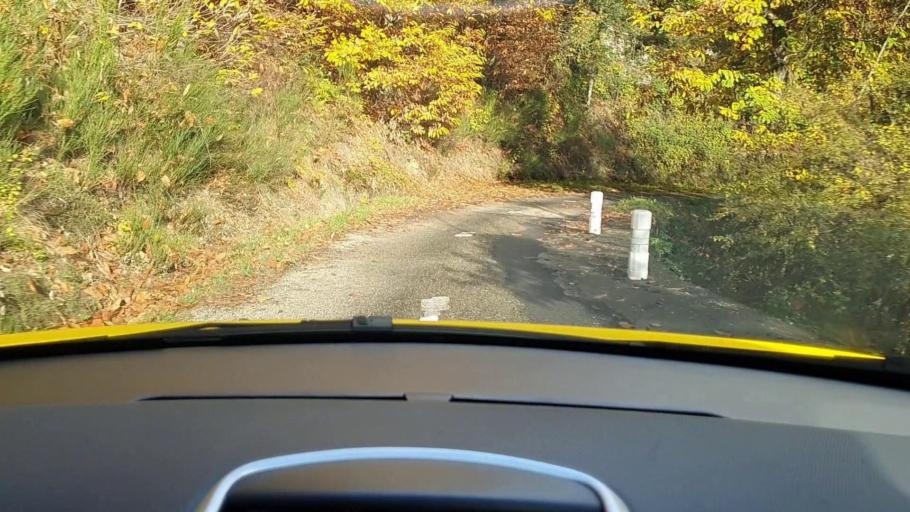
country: FR
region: Languedoc-Roussillon
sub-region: Departement du Gard
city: Valleraugue
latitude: 44.0869
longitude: 3.7424
